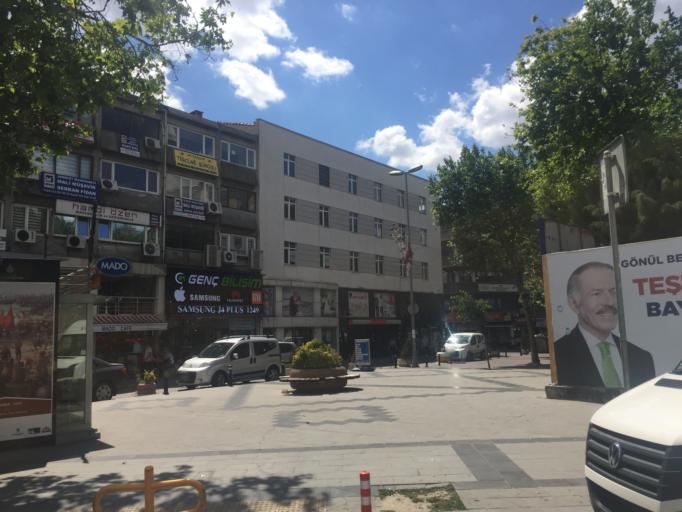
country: TR
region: Istanbul
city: merter keresteciler
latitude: 41.0347
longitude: 28.9119
